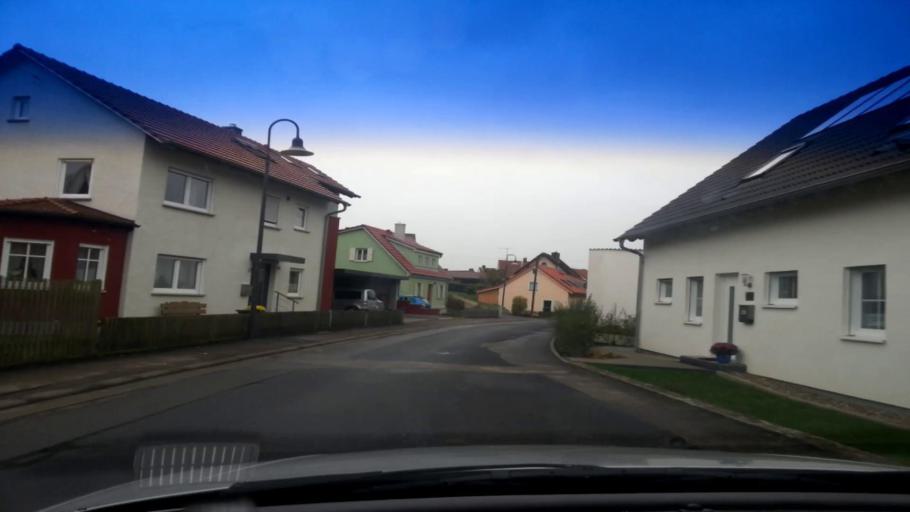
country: DE
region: Bavaria
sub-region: Upper Franconia
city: Litzendorf
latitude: 49.8997
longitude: 11.0291
